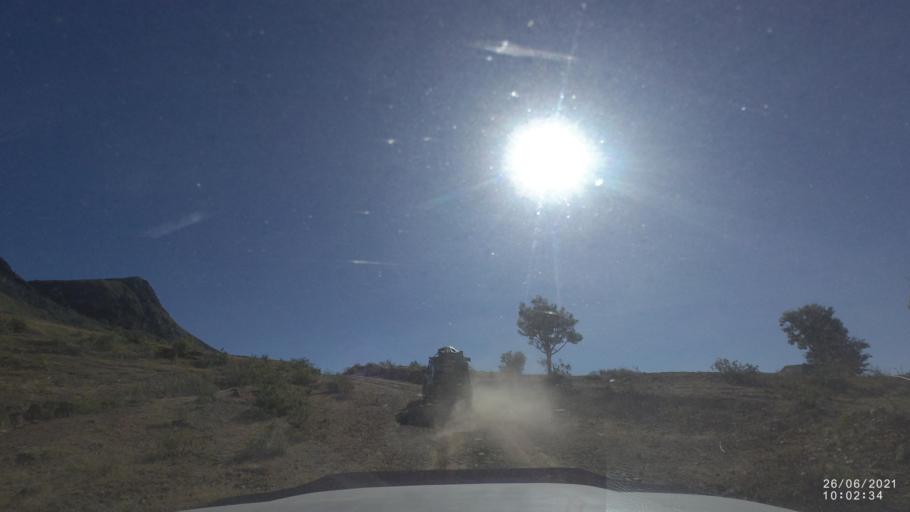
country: BO
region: Cochabamba
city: Mizque
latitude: -17.9258
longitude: -65.6273
